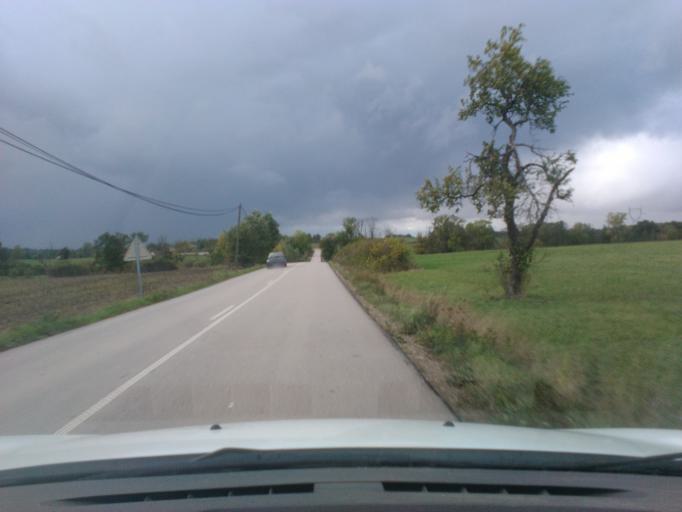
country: FR
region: Lorraine
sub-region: Departement des Vosges
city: Deyvillers
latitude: 48.2608
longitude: 6.5288
